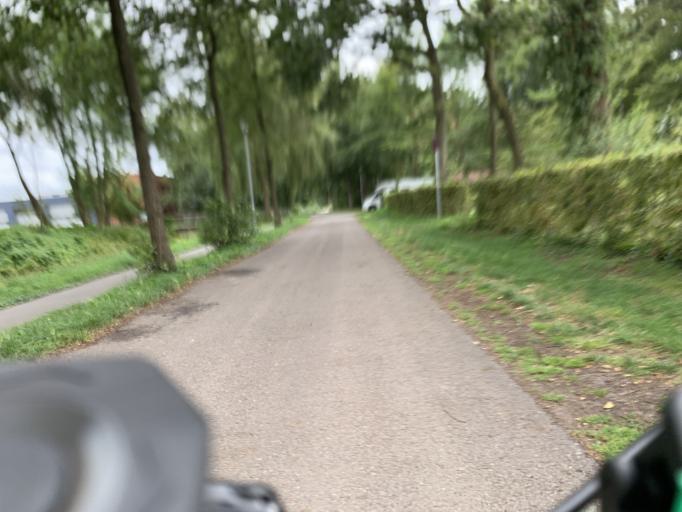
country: DE
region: Lower Saxony
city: Westerstede
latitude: 53.2559
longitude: 7.9151
